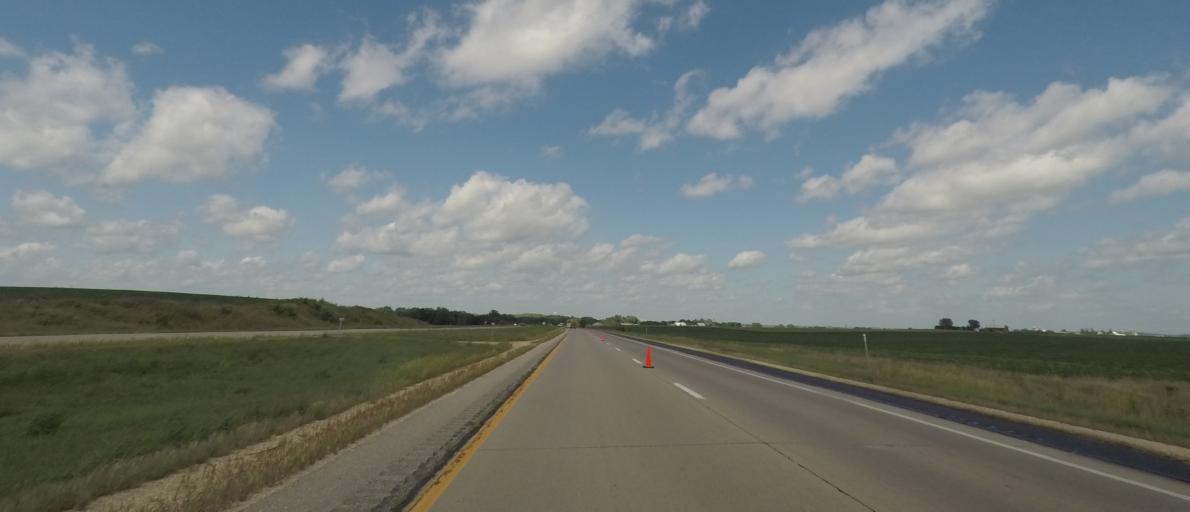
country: US
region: Iowa
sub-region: Jones County
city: Monticello
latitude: 42.1866
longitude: -91.2196
